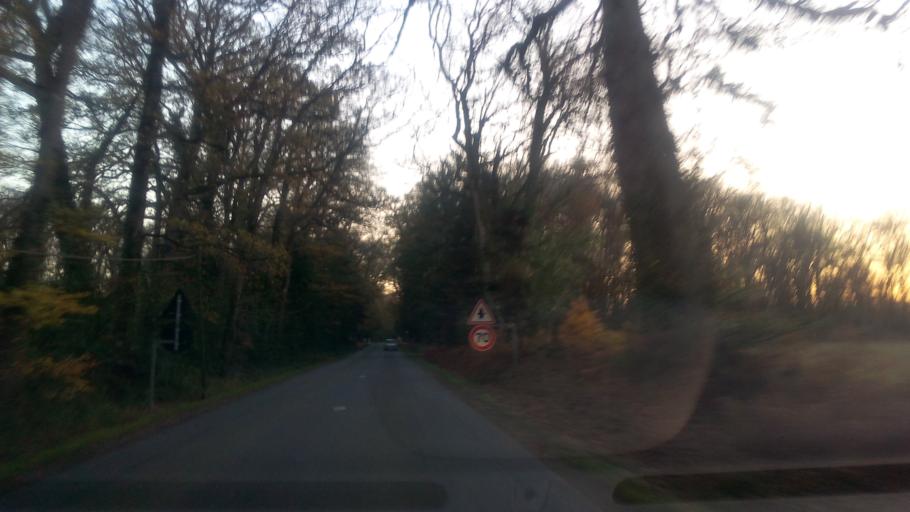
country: FR
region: Brittany
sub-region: Departement d'Ille-et-Vilaine
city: Bains-sur-Oust
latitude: 47.7080
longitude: -2.0533
